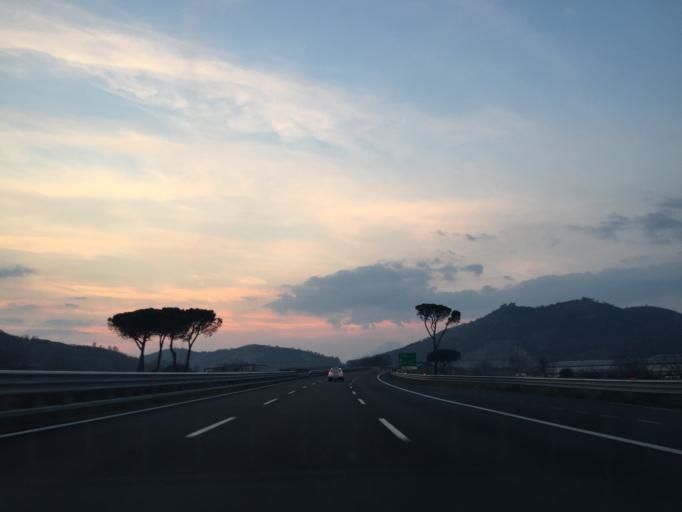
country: IT
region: Campania
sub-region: Provincia di Salerno
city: Casali-San Potito
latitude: 40.7676
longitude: 14.6791
